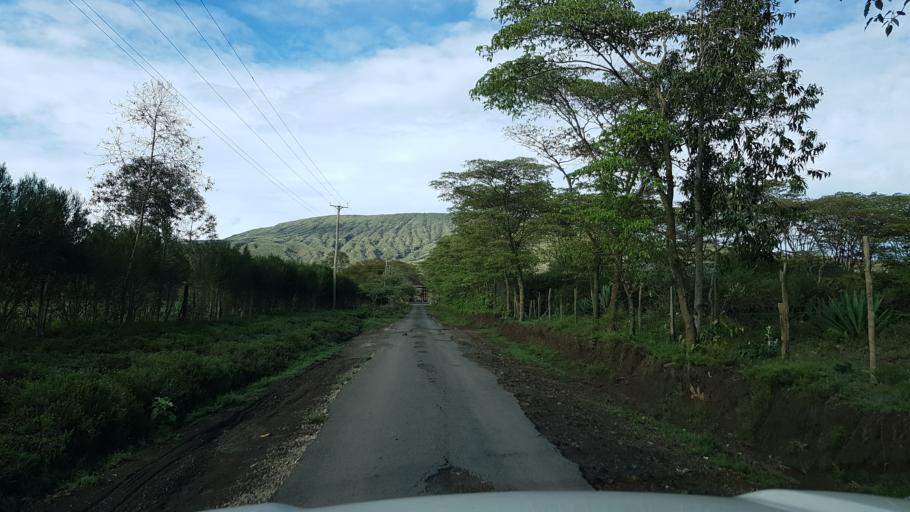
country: KE
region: Nakuru
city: Kijabe
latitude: -0.8872
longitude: 36.4757
